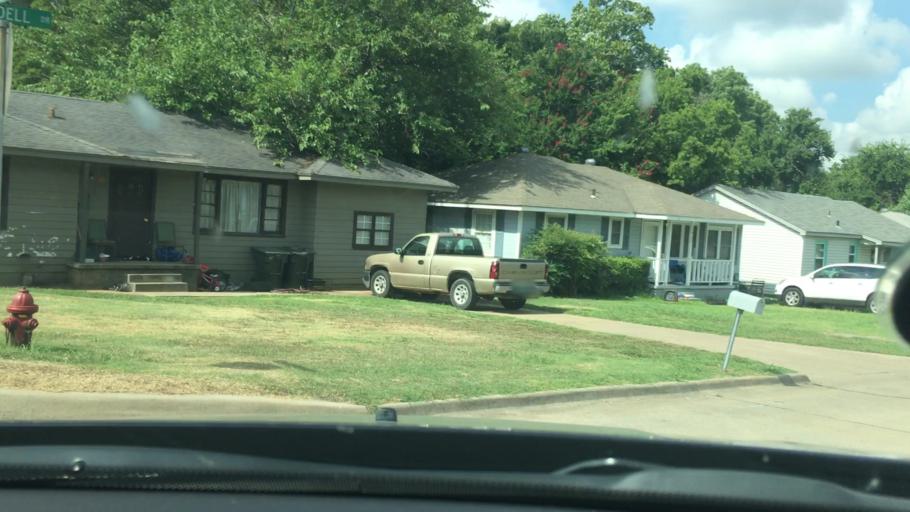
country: US
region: Oklahoma
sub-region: Bryan County
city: Durant
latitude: 34.0044
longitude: -96.3905
